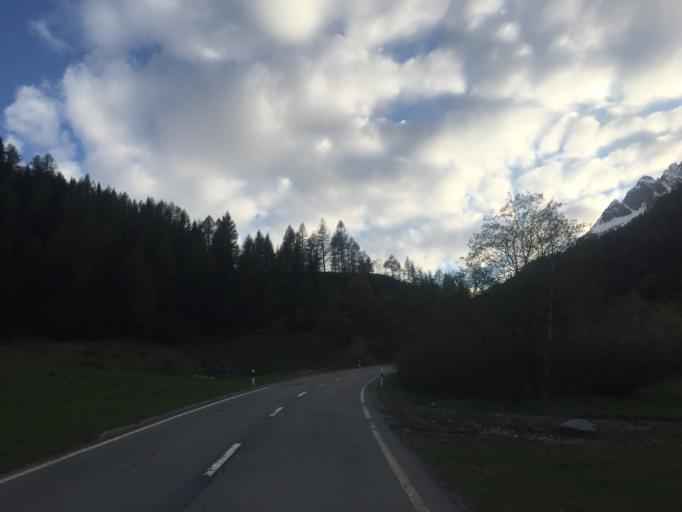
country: CH
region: Ticino
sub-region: Leventina District
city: Airolo
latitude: 46.4978
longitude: 8.5014
